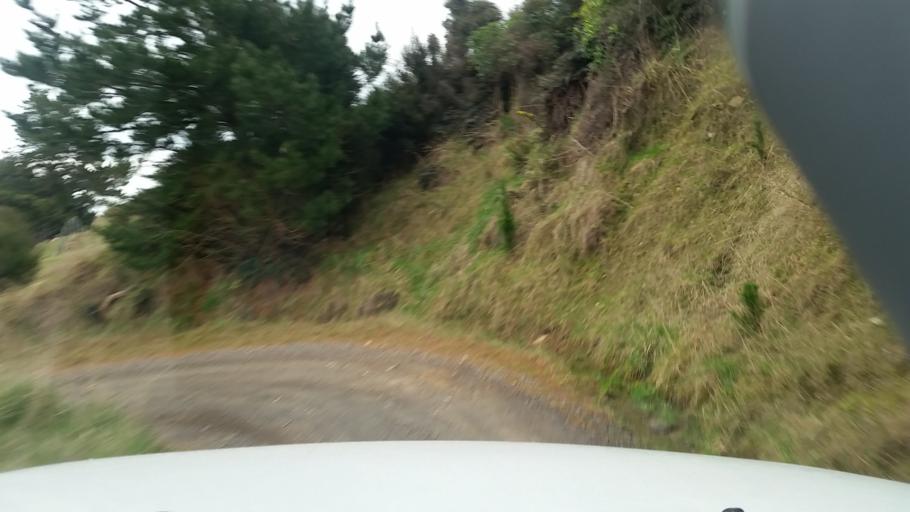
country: NZ
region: Canterbury
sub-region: Christchurch City
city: Christchurch
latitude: -43.7818
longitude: 172.8106
